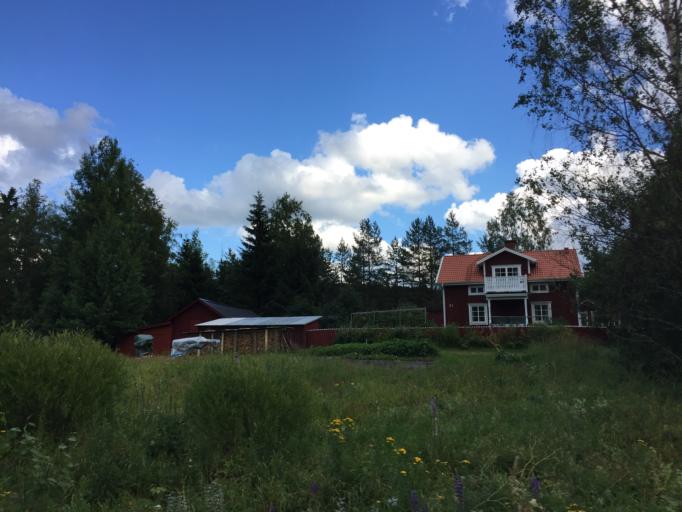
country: SE
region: Gaevleborg
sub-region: Ljusdals Kommun
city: Jaervsoe
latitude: 61.7211
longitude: 16.2905
